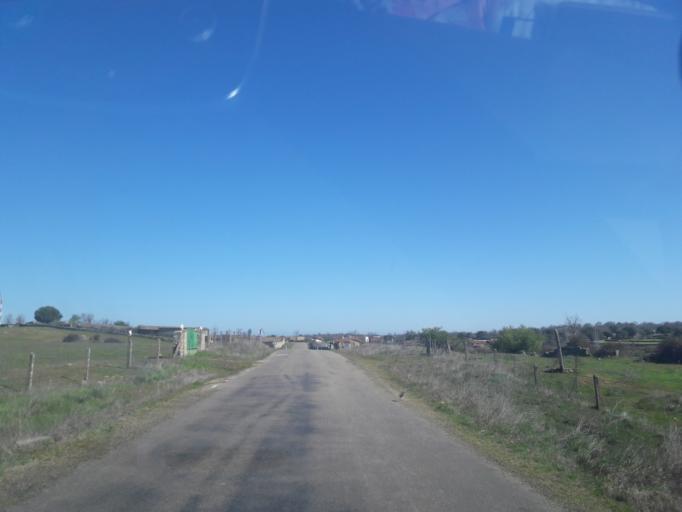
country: ES
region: Castille and Leon
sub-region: Provincia de Salamanca
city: Valsalabroso
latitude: 41.1480
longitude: -6.4861
